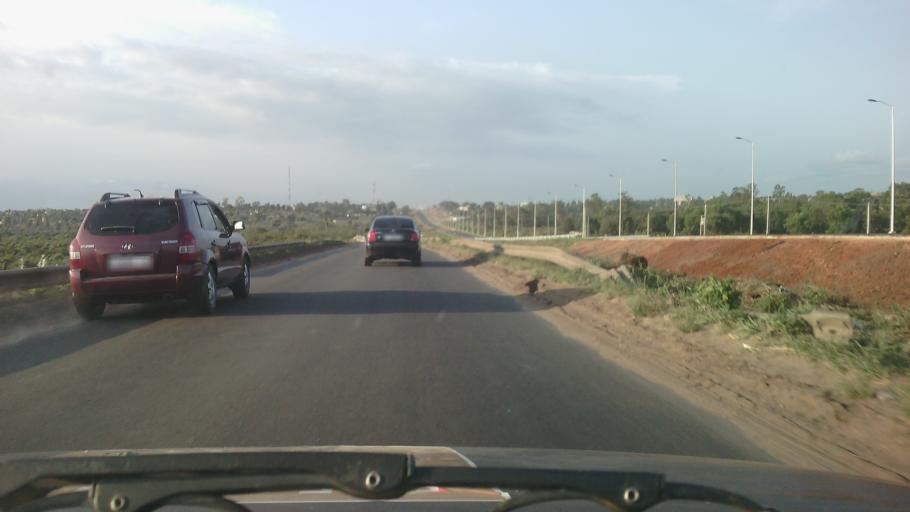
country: TG
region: Maritime
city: Tsevie
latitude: 6.3062
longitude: 1.2152
